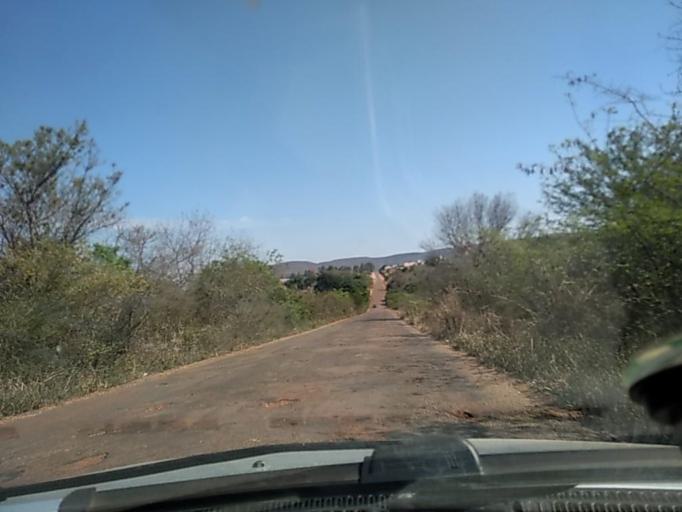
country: BR
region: Bahia
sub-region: Caetite
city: Caetite
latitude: -14.0428
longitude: -42.4859
